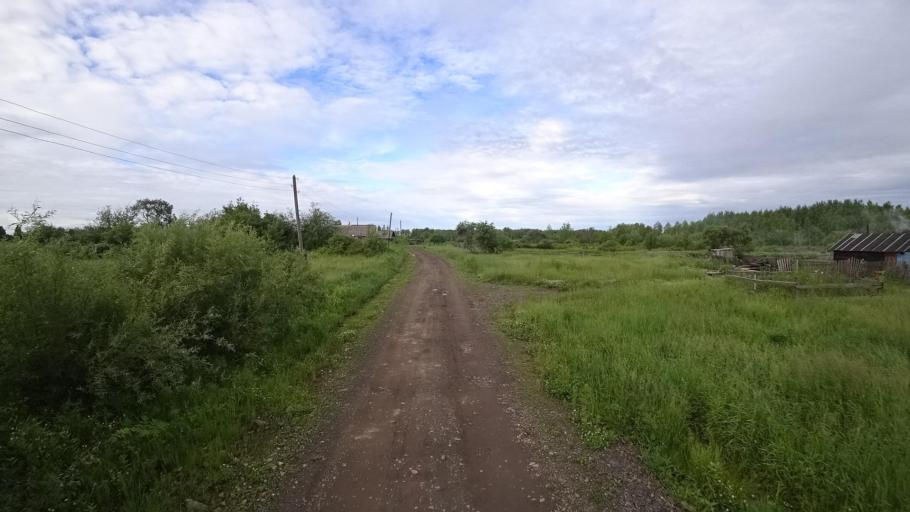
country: RU
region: Khabarovsk Krai
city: Amursk
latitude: 49.8841
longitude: 136.1282
